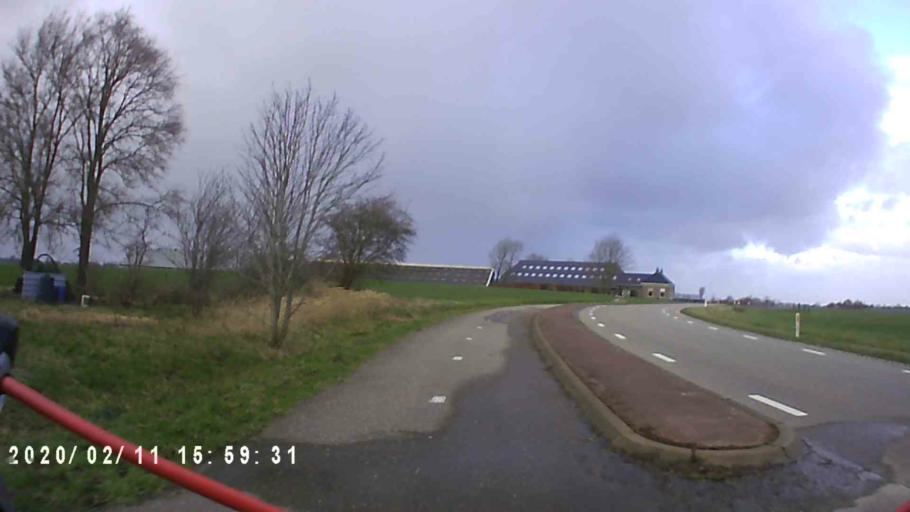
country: NL
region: Groningen
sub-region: Gemeente Zuidhorn
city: Oldehove
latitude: 53.2907
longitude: 6.4212
